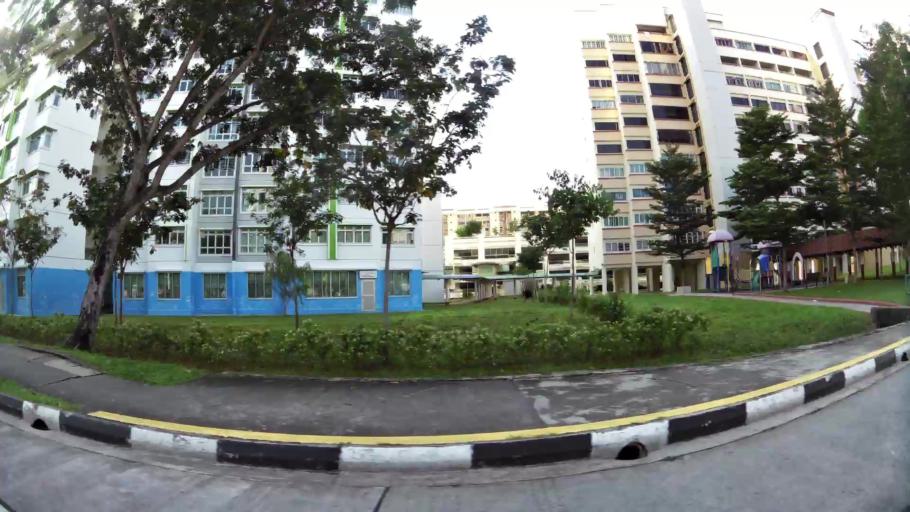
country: SG
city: Singapore
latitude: 1.3283
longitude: 103.9230
